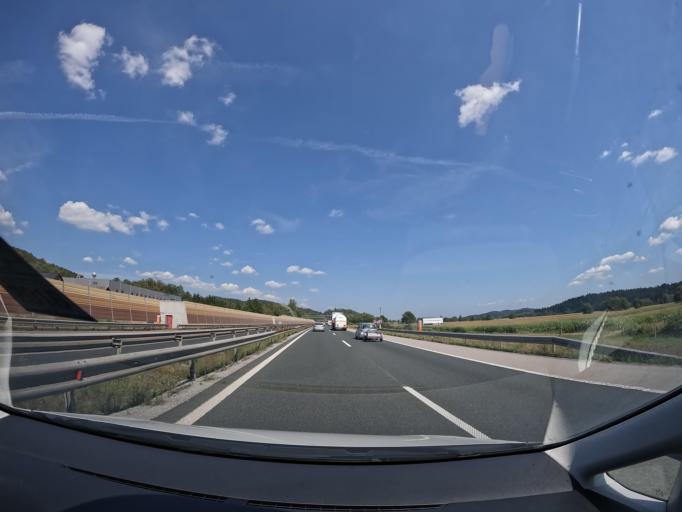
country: SI
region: Log-Dragomer
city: Log pri Brezovici
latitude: 46.0003
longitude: 14.3453
